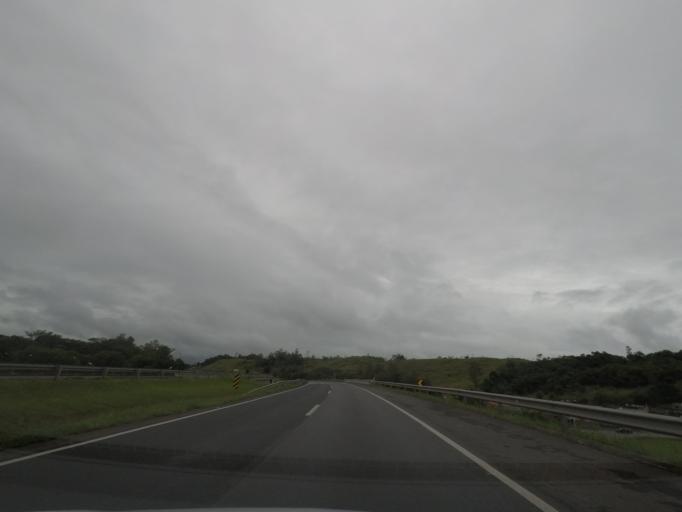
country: BR
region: Sao Paulo
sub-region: Cajati
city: Cajati
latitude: -24.7311
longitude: -48.0995
